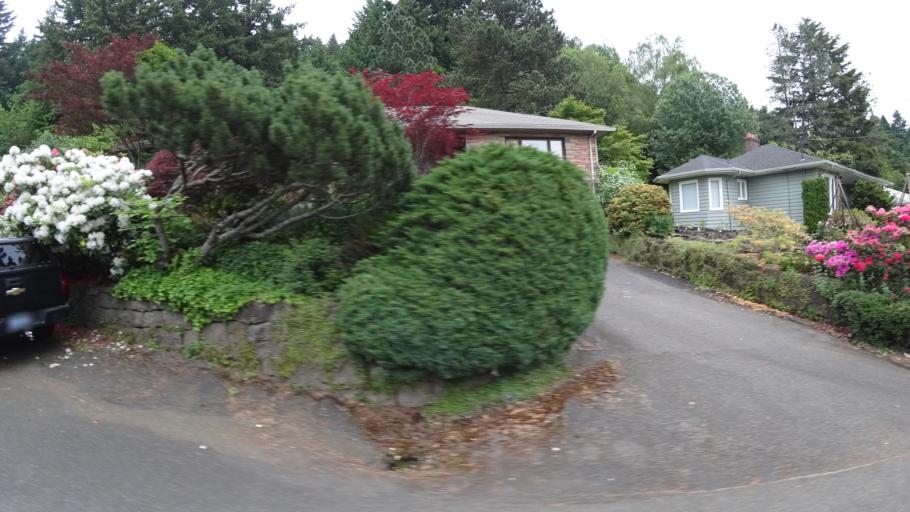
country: US
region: Oregon
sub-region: Multnomah County
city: Portland
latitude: 45.4882
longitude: -122.7006
